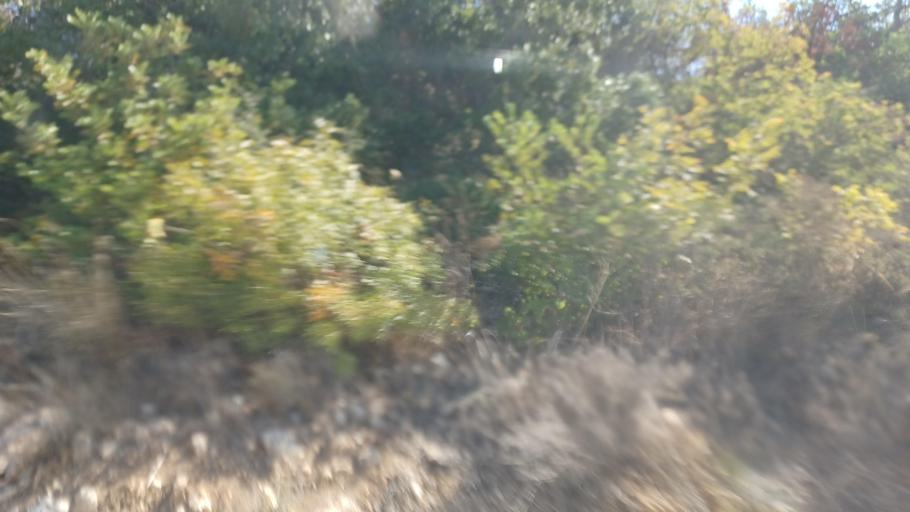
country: CY
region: Pafos
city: Polis
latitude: 34.9864
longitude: 32.4936
